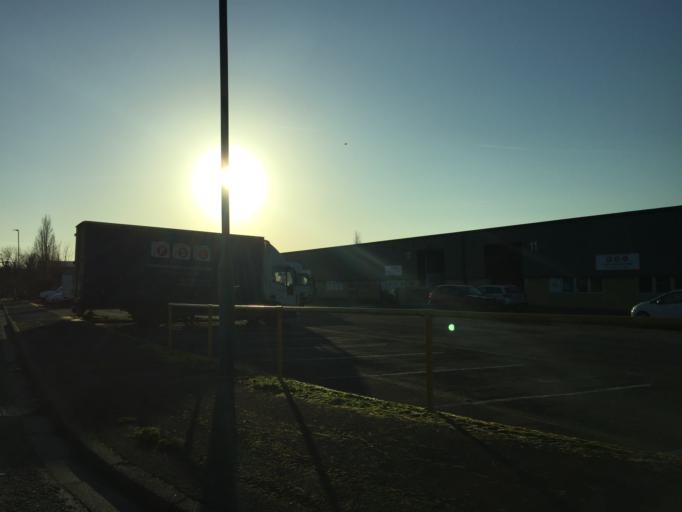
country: GB
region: England
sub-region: Gloucestershire
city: Stonehouse
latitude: 51.7495
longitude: -2.2933
